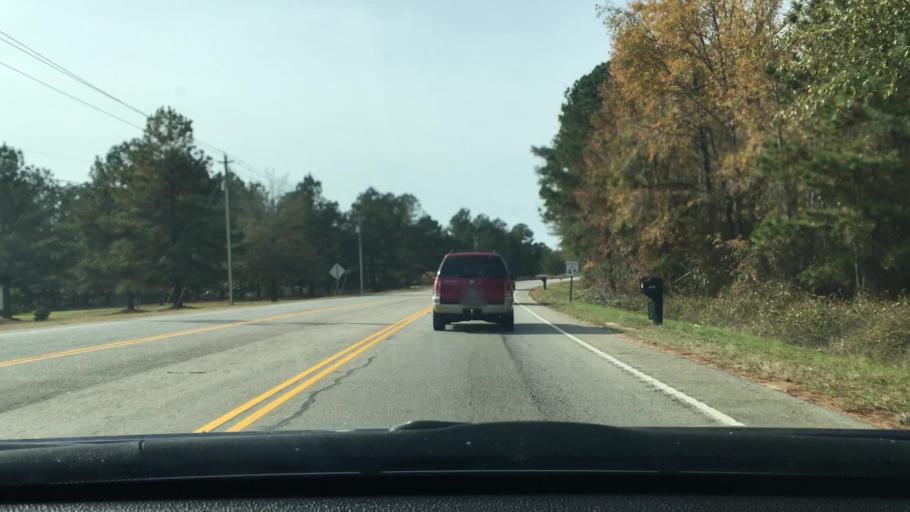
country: US
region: South Carolina
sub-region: Sumter County
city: Cherryvale
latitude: 33.9364
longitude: -80.4545
